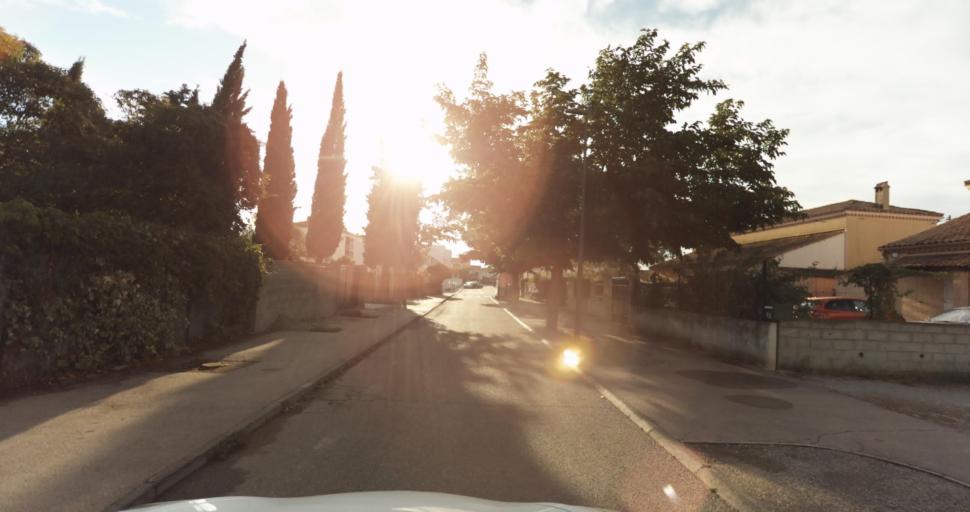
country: FR
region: Provence-Alpes-Cote d'Azur
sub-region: Departement des Bouches-du-Rhone
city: Miramas
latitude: 43.5864
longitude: 4.9997
